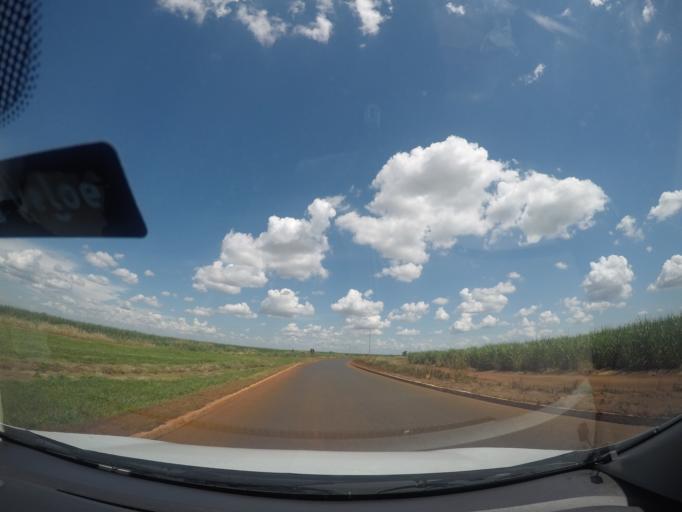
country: BR
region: Minas Gerais
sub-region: Frutal
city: Frutal
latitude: -19.8193
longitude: -48.7319
